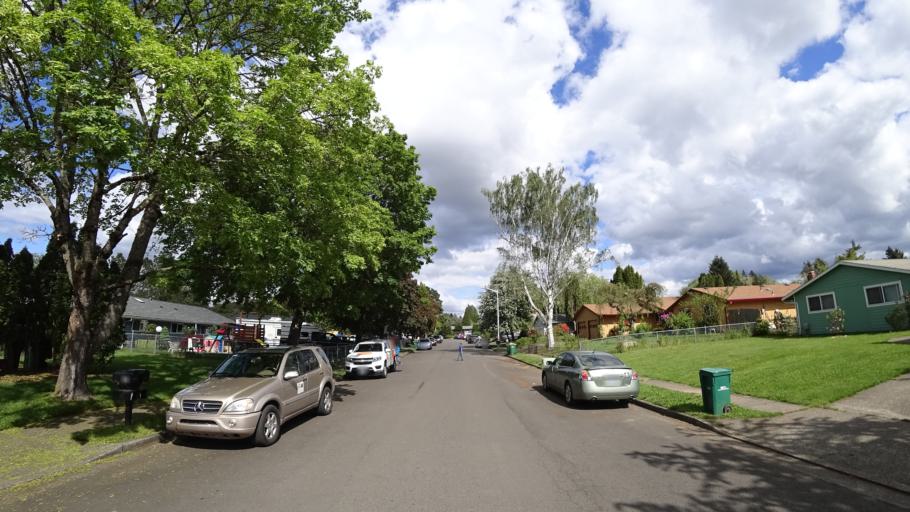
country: US
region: Oregon
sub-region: Washington County
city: Beaverton
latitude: 45.4812
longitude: -122.8209
